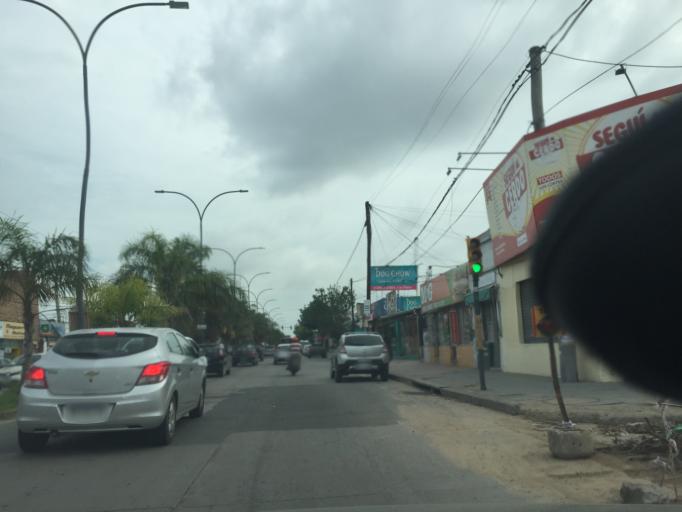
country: AR
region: Cordoba
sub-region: Departamento de Capital
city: Cordoba
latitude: -31.4482
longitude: -64.1993
